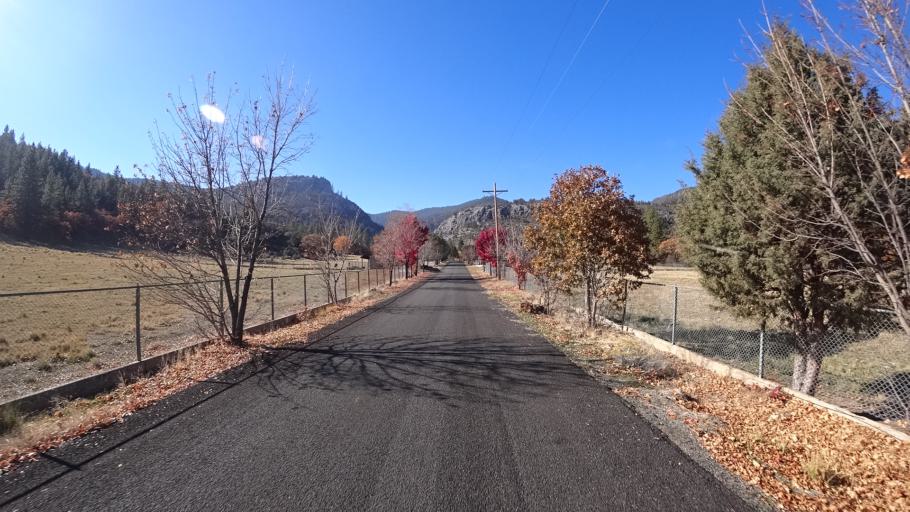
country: US
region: California
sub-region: Siskiyou County
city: Weed
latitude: 41.5032
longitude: -122.5878
